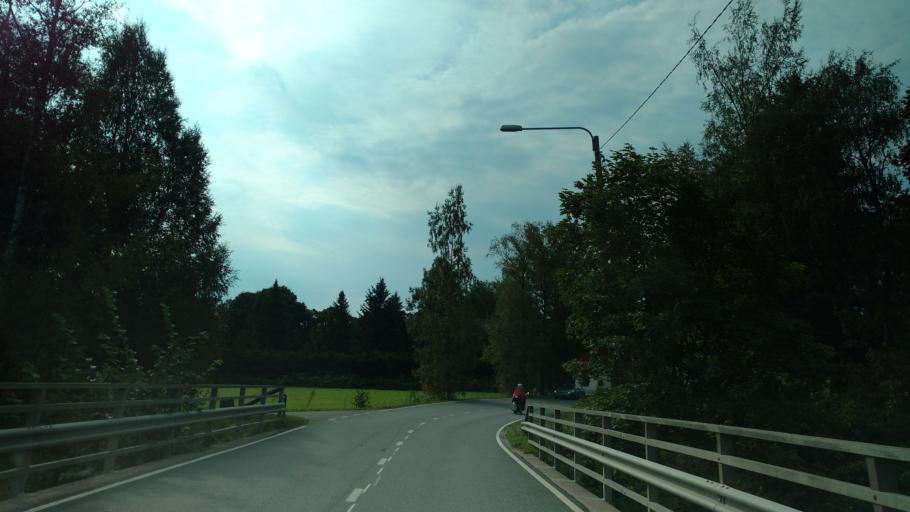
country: FI
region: Varsinais-Suomi
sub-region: Loimaa
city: Koski Tl
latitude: 60.6607
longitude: 23.1481
